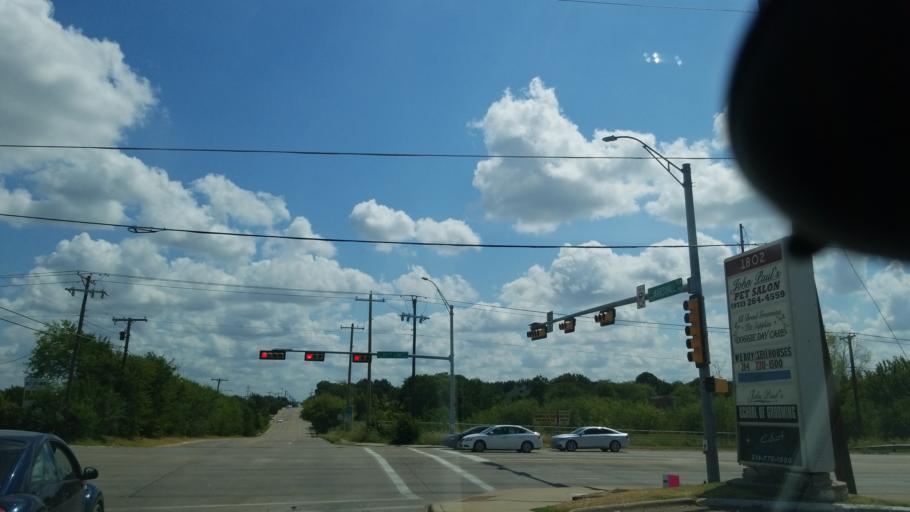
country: US
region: Texas
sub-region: Dallas County
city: Grand Prairie
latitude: 32.7205
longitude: -96.9945
